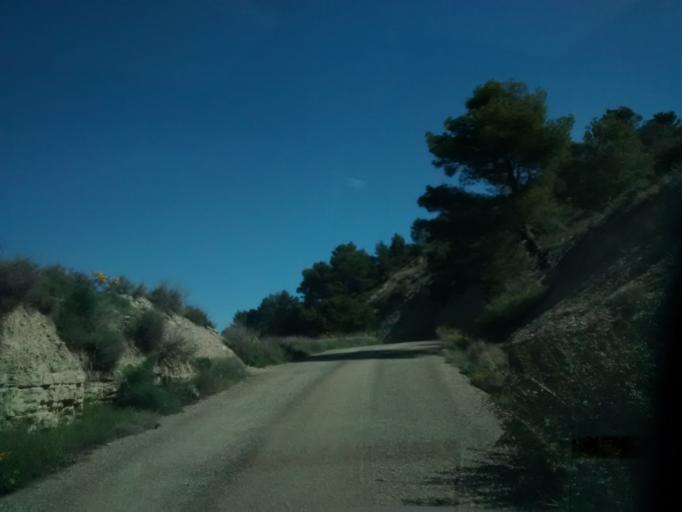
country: ES
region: Aragon
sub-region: Provincia de Huesca
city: Alcubierre
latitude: 41.8284
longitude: -0.5170
